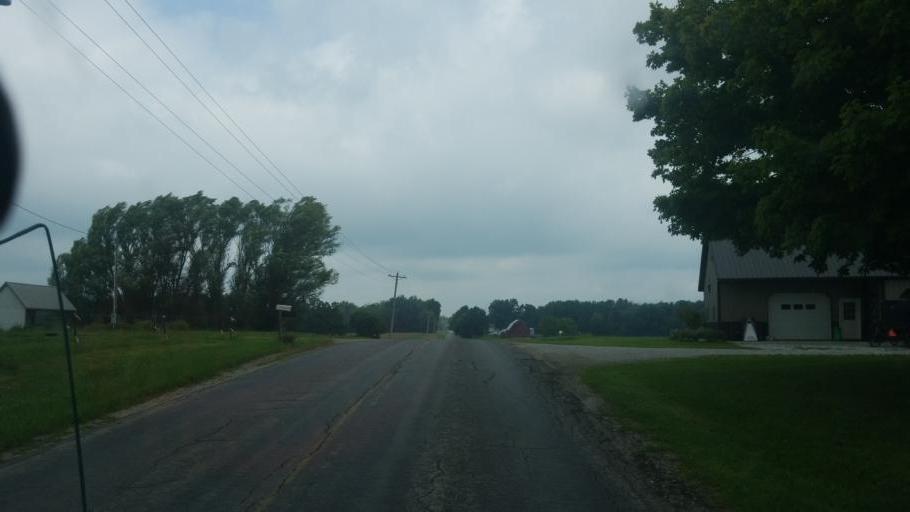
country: US
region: Ohio
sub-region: Huron County
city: Greenwich
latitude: 40.9779
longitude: -82.4718
